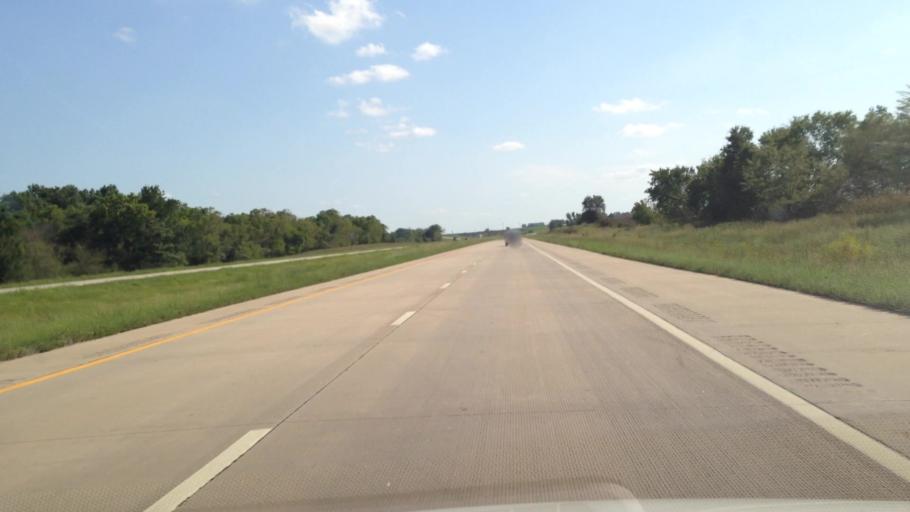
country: US
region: Kansas
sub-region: Bourbon County
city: Fort Scott
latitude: 37.9034
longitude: -94.7037
